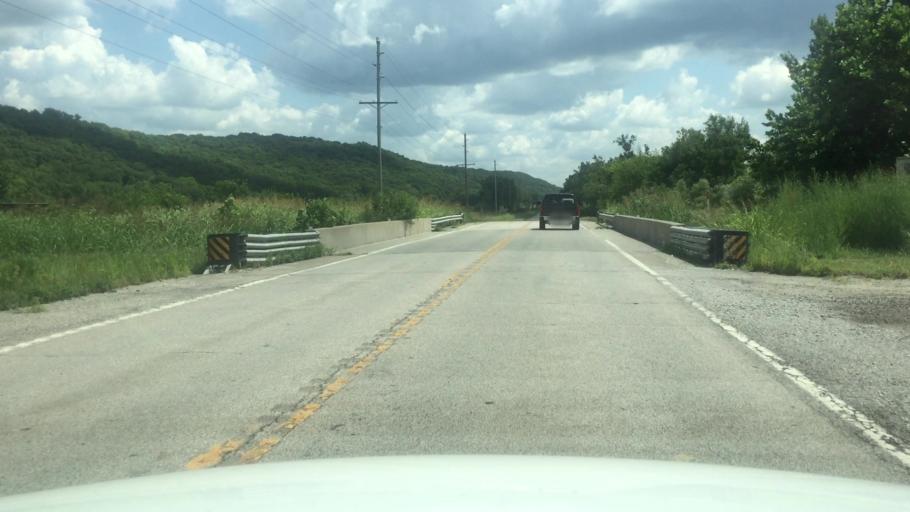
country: US
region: Kansas
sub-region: Atchison County
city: Atchison
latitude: 39.5063
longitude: -95.0118
